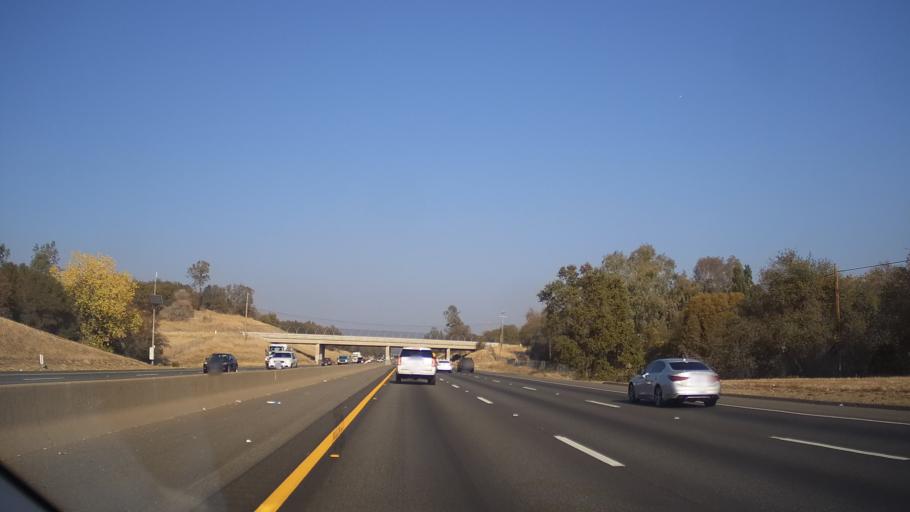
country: US
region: California
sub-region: Placer County
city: Newcastle
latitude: 38.8530
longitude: -121.1456
